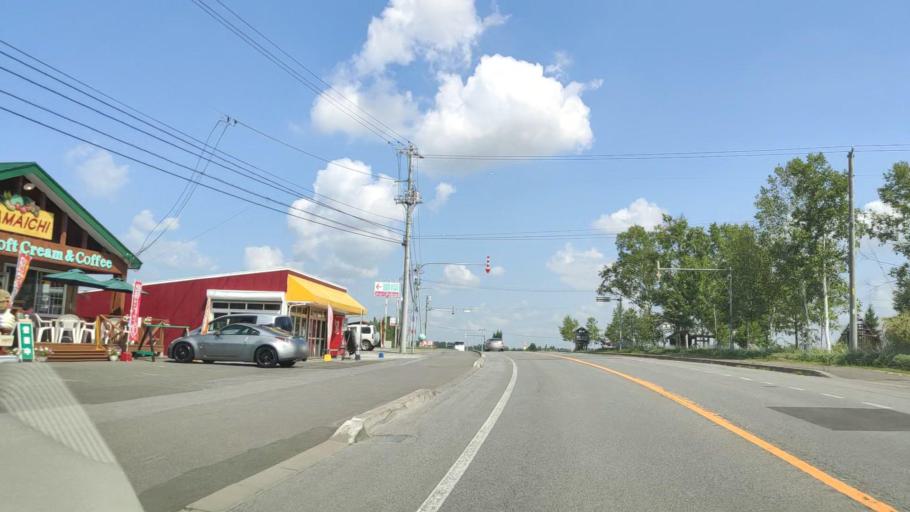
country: JP
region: Hokkaido
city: Shimo-furano
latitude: 43.5189
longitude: 142.4483
